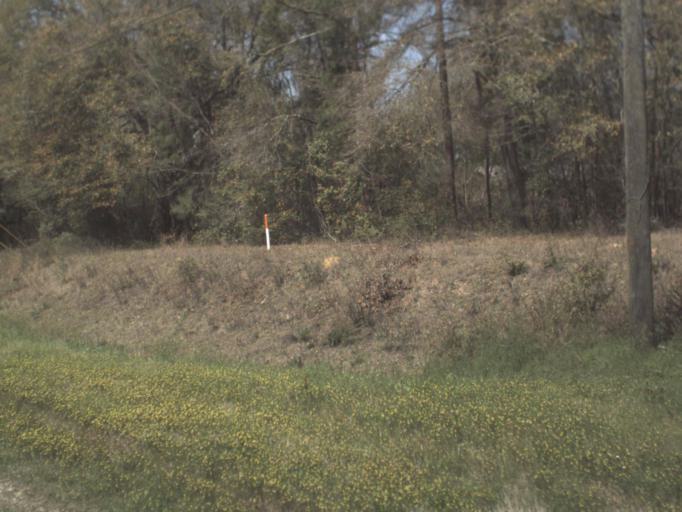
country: US
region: Florida
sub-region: Gadsden County
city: Quincy
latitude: 30.5614
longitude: -84.5377
